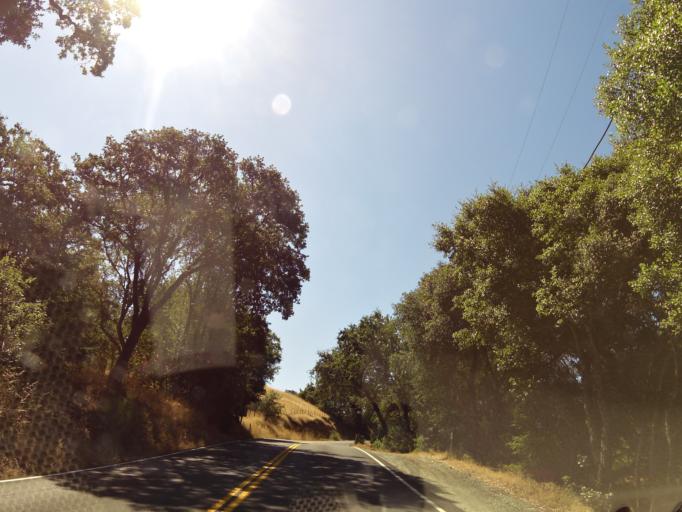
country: US
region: California
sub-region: Sonoma County
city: Cloverdale
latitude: 38.8836
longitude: -123.1171
